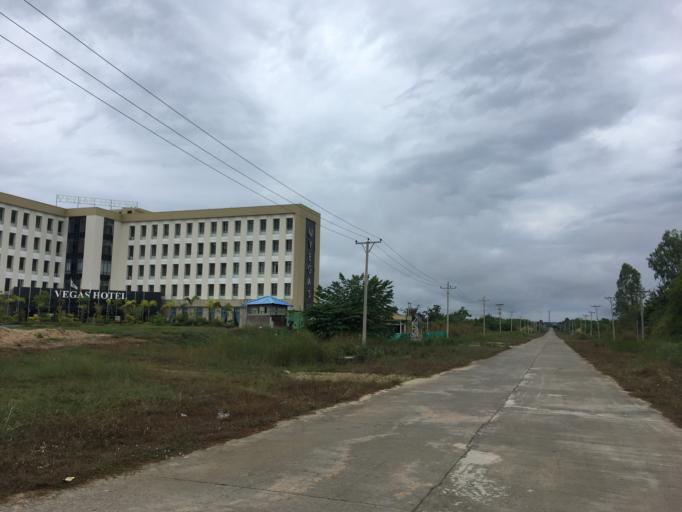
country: MM
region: Mandalay
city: Nay Pyi Taw
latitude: 19.6961
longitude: 96.1215
